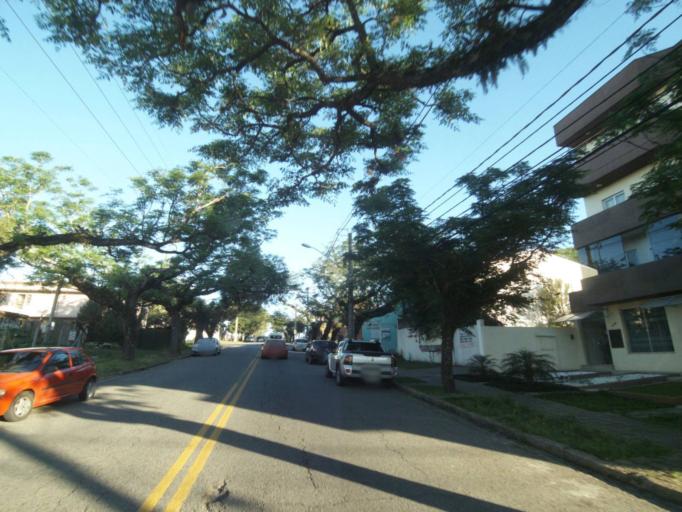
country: BR
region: Parana
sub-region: Curitiba
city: Curitiba
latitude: -25.3897
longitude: -49.2421
